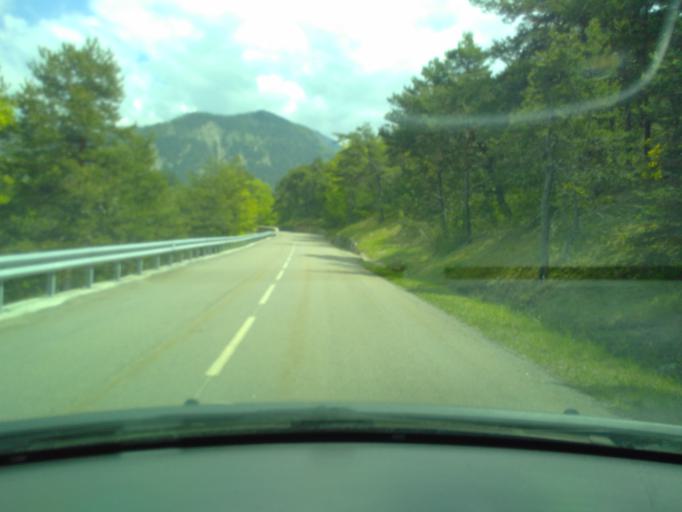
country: FR
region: Rhone-Alpes
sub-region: Departement de la Drome
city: Die
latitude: 44.6483
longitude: 5.4455
